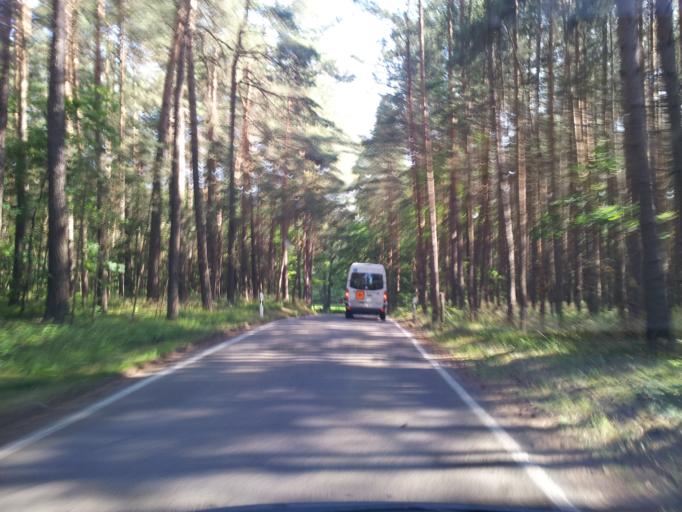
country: DE
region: Saxony
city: Hockendorf
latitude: 51.2031
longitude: 13.9019
